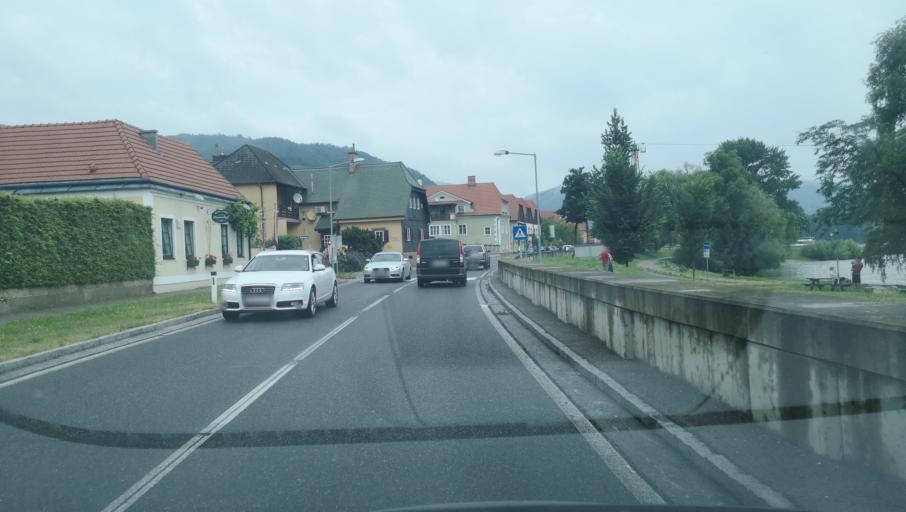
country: AT
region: Lower Austria
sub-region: Politischer Bezirk Krems
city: Weinzierl am Walde
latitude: 48.3937
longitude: 15.4690
